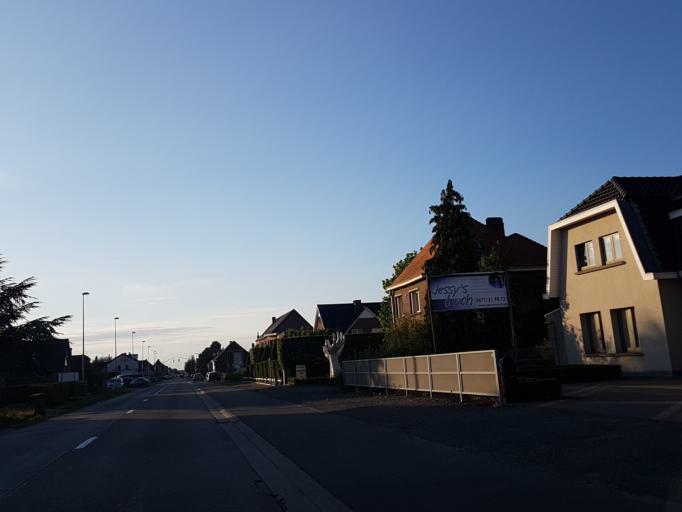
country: BE
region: Flanders
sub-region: Provincie Oost-Vlaanderen
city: Lebbeke
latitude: 50.9801
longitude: 4.1424
